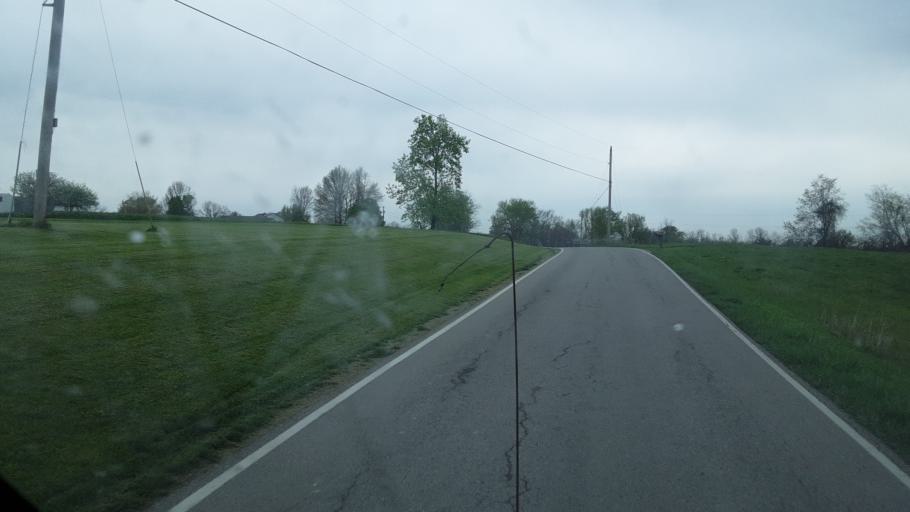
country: US
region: Kentucky
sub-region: Owen County
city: Owenton
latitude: 38.6496
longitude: -84.7719
